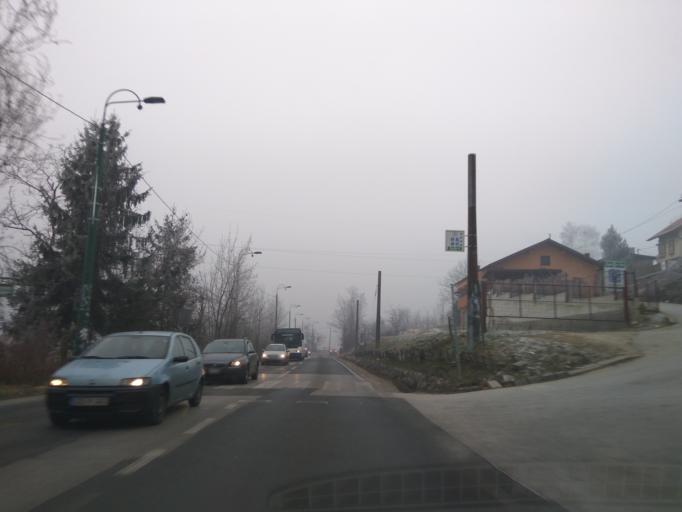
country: BA
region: Federation of Bosnia and Herzegovina
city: Hotonj
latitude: 43.8896
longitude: 18.3821
